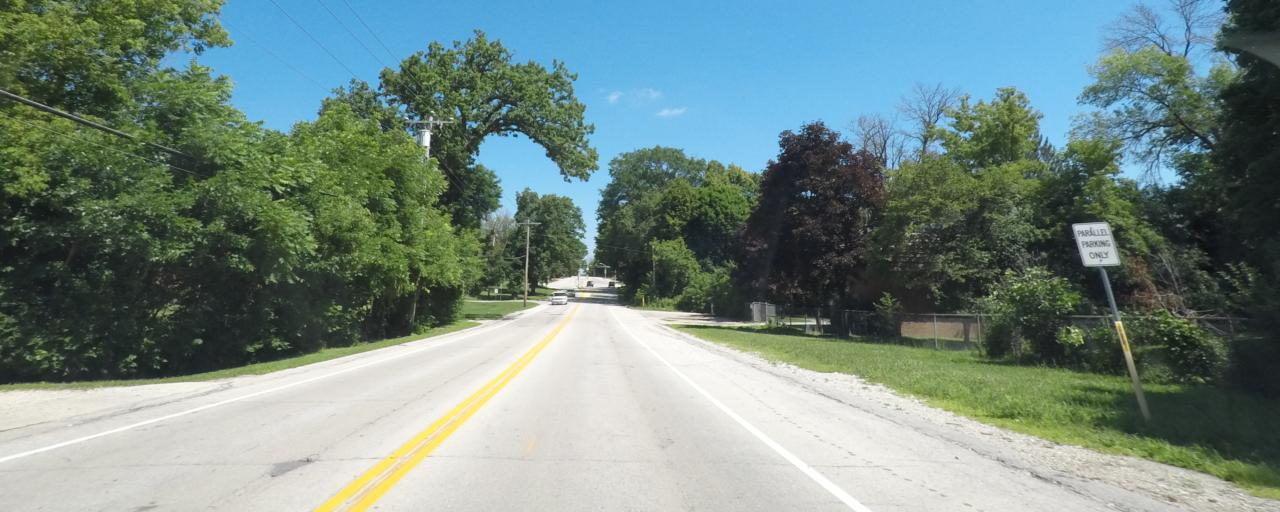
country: US
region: Wisconsin
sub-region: Waukesha County
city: Elm Grove
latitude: 43.0144
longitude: -88.0673
